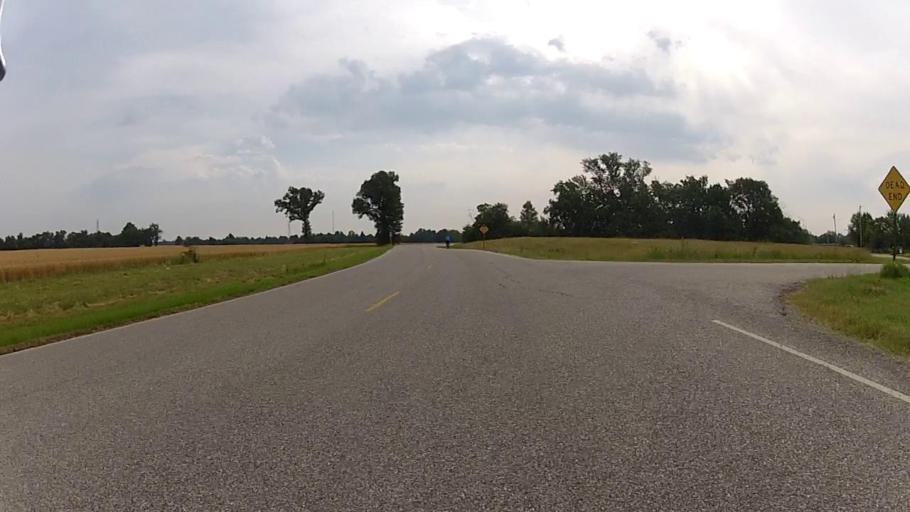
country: US
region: Kansas
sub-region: Cherokee County
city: Baxter Springs
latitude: 37.0753
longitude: -94.7189
